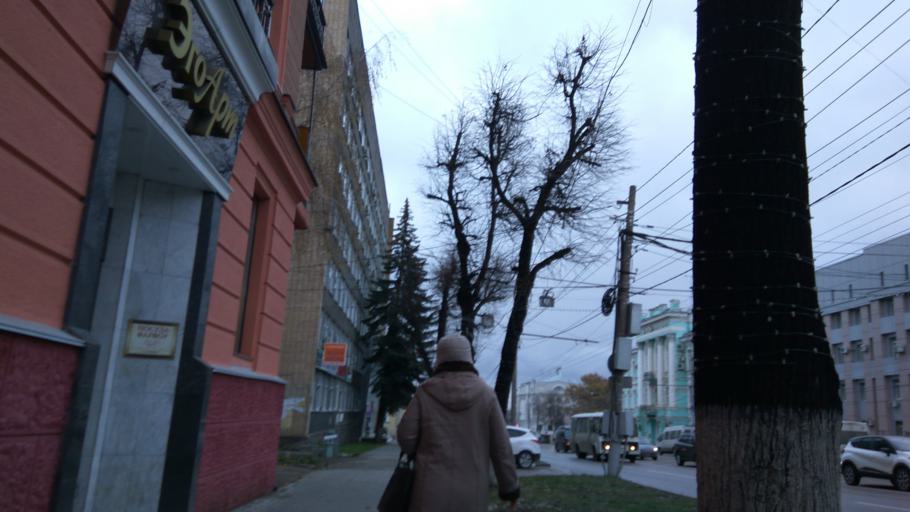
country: RU
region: Tula
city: Tula
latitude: 54.1841
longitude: 37.6072
